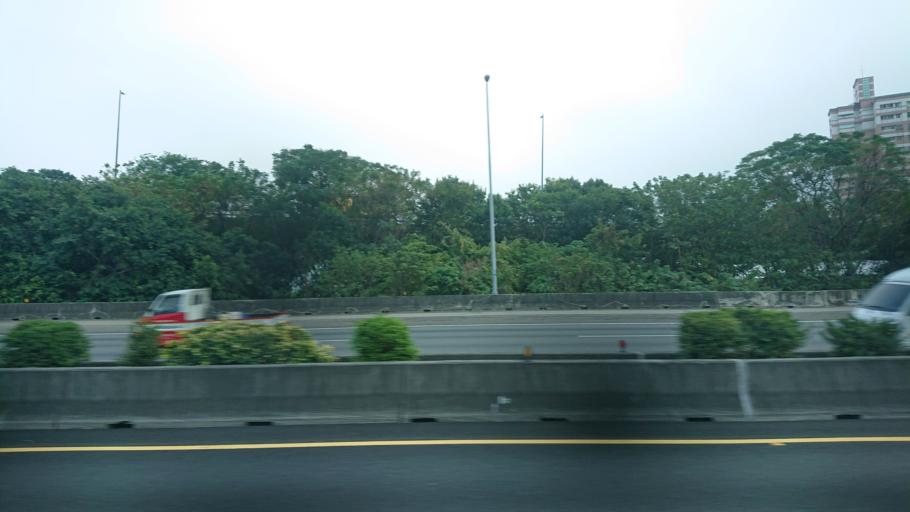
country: TW
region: Taiwan
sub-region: Changhua
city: Chang-hua
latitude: 24.0993
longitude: 120.5536
